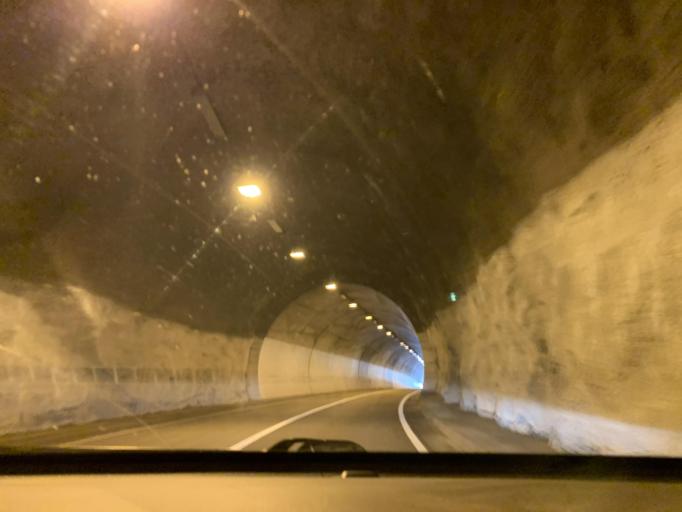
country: IT
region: Trentino-Alto Adige
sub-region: Bolzano
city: Avelengo
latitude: 46.6468
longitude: 11.2244
